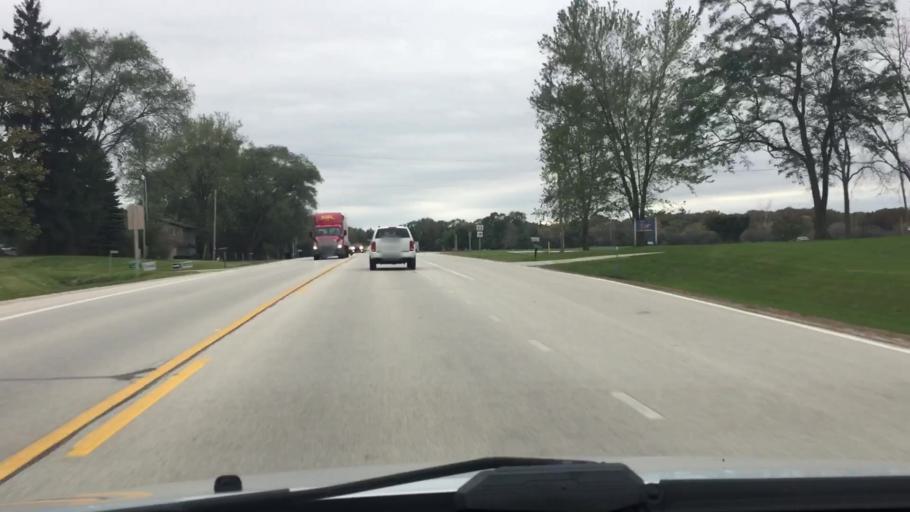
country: US
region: Wisconsin
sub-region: Waukesha County
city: North Prairie
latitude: 42.9445
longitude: -88.3764
